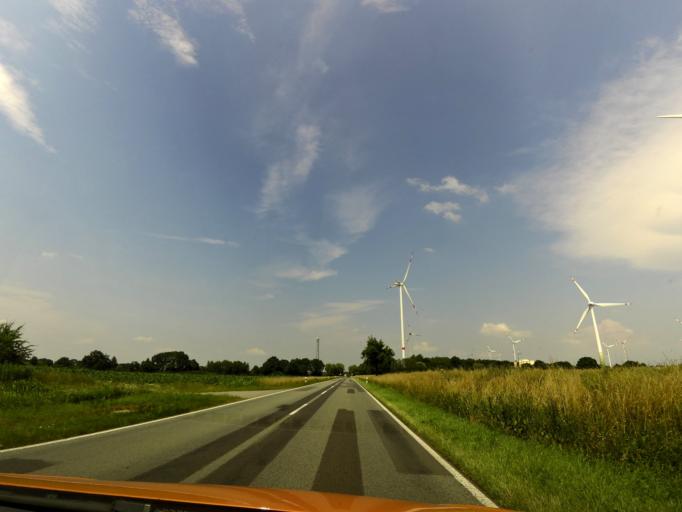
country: DE
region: Brandenburg
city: Gerdshagen
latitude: 53.2248
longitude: 12.2050
